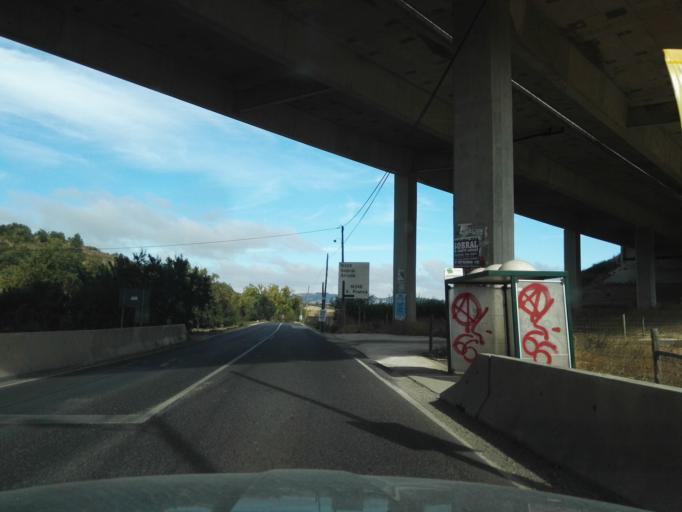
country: PT
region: Lisbon
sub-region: Arruda Dos Vinhos
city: Arruda dos Vinhos
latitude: 38.9647
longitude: -9.0628
